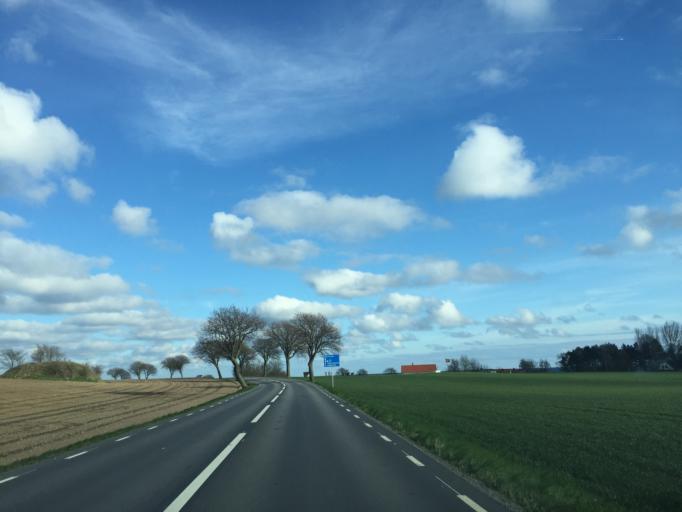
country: SE
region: Skane
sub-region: Skurups Kommun
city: Skivarp
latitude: 55.4192
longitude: 13.6304
